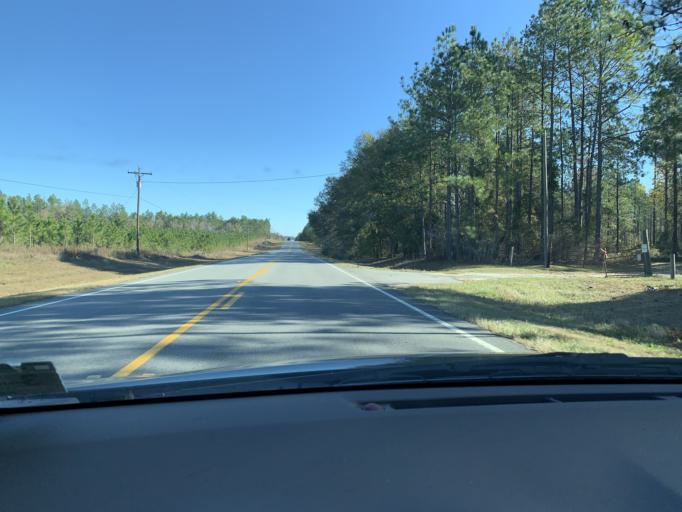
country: US
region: Georgia
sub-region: Ben Hill County
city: Fitzgerald
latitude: 31.7634
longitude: -83.1129
